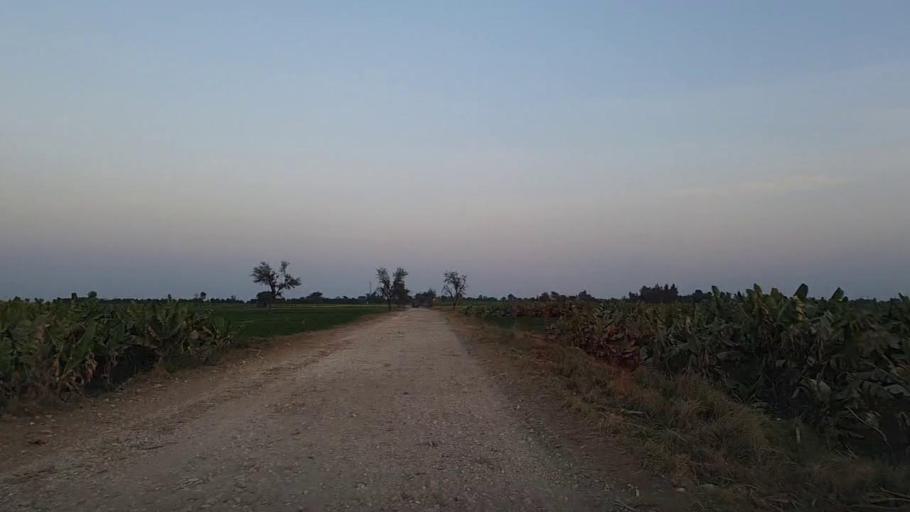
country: PK
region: Sindh
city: Tando Mittha Khan
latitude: 25.9452
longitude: 69.1482
